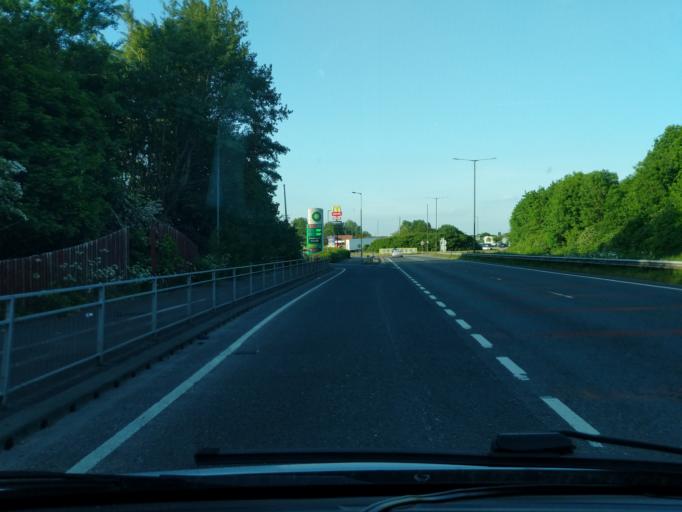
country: GB
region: England
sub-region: St. Helens
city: St Helens
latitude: 53.4407
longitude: -2.7318
